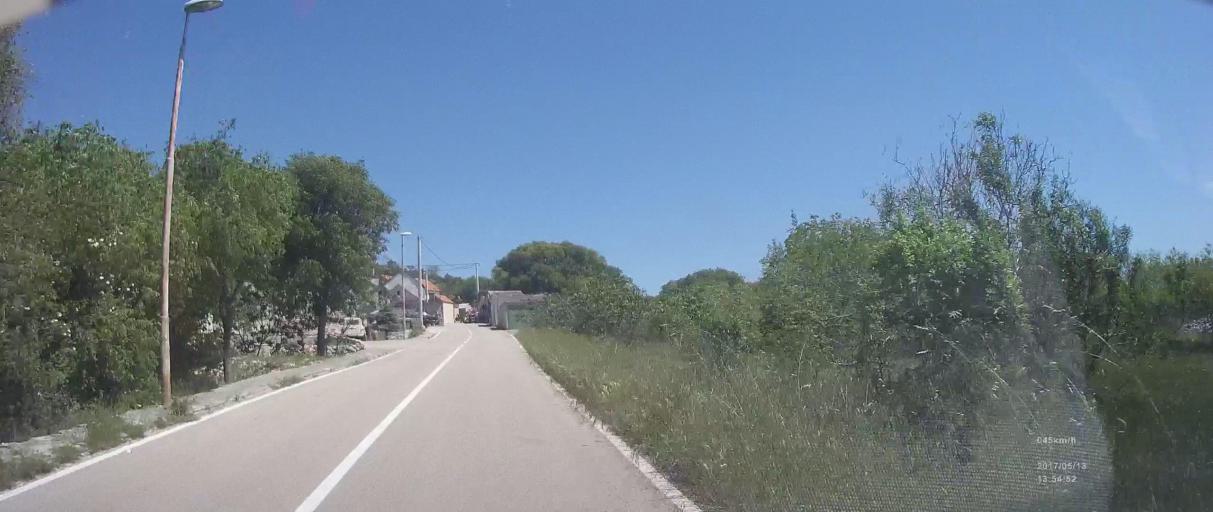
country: HR
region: Sibensko-Kniniska
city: Rogoznica
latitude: 43.5962
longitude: 16.0112
